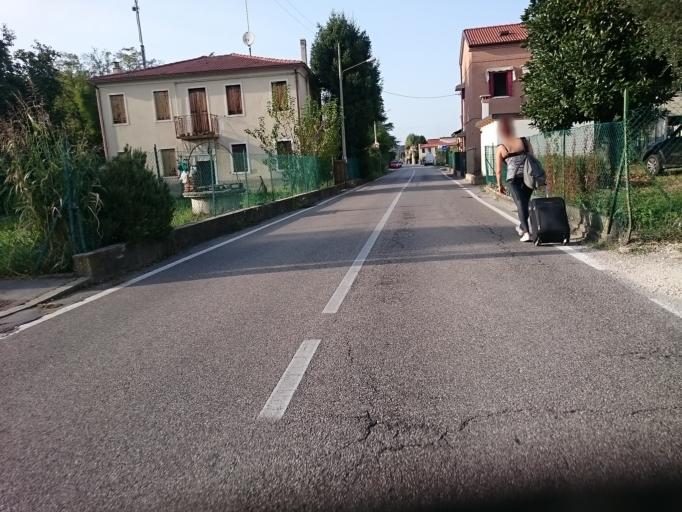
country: IT
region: Veneto
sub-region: Provincia di Padova
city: Padova
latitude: 45.3984
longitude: 11.9032
